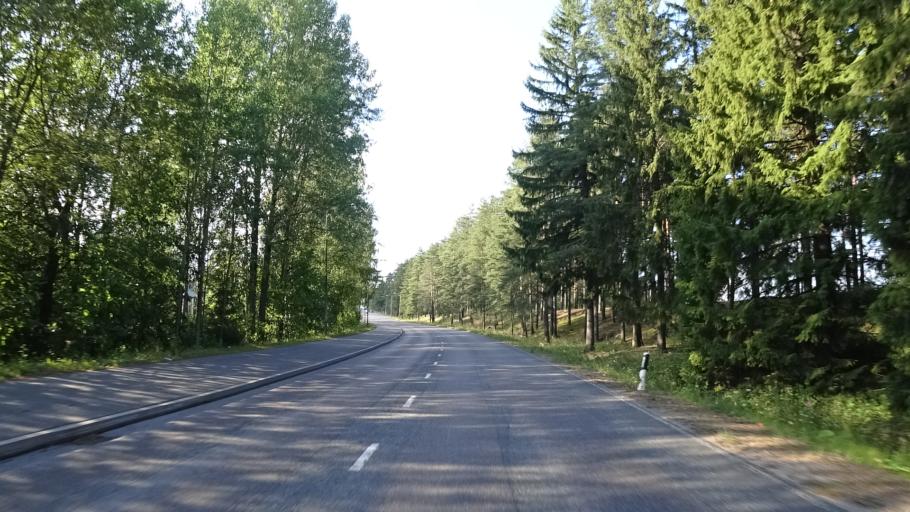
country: FI
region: South Karelia
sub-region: Imatra
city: Imatra
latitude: 61.1804
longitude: 28.7819
